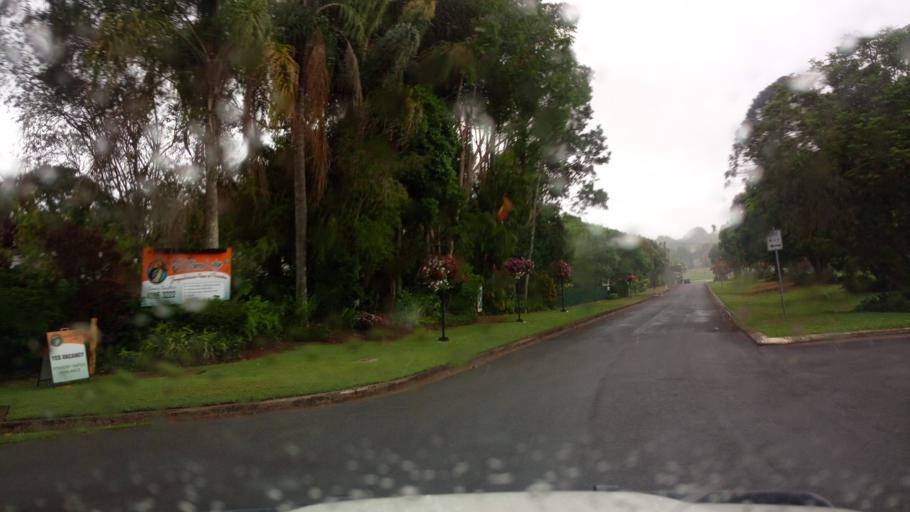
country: AU
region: Queensland
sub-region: Tablelands
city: Tolga
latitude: -17.2684
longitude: 145.5811
